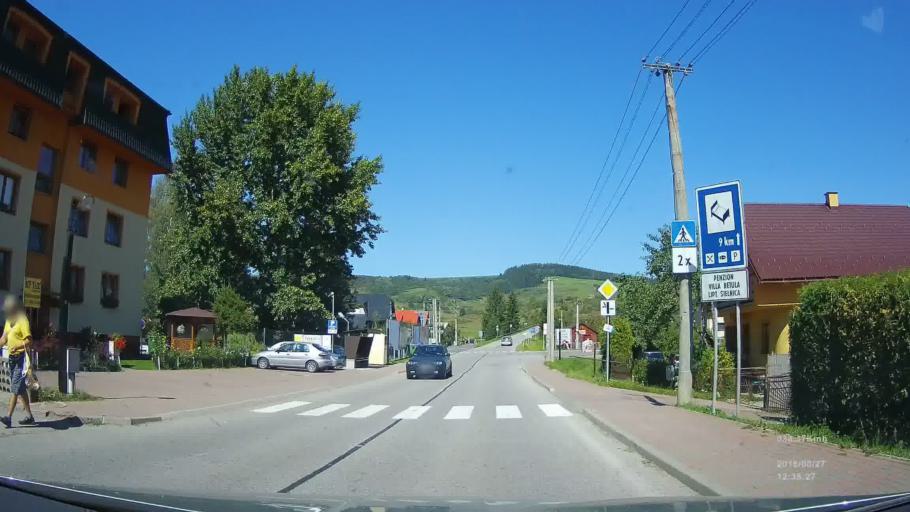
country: SK
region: Zilinsky
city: Ruzomberok
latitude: 49.0995
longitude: 19.4348
